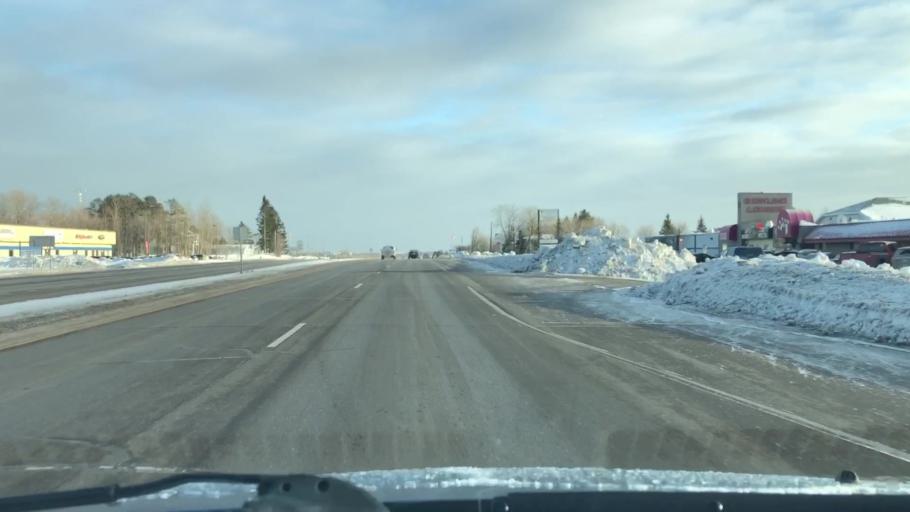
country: US
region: Minnesota
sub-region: Saint Louis County
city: Hermantown
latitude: 46.8270
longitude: -92.1951
